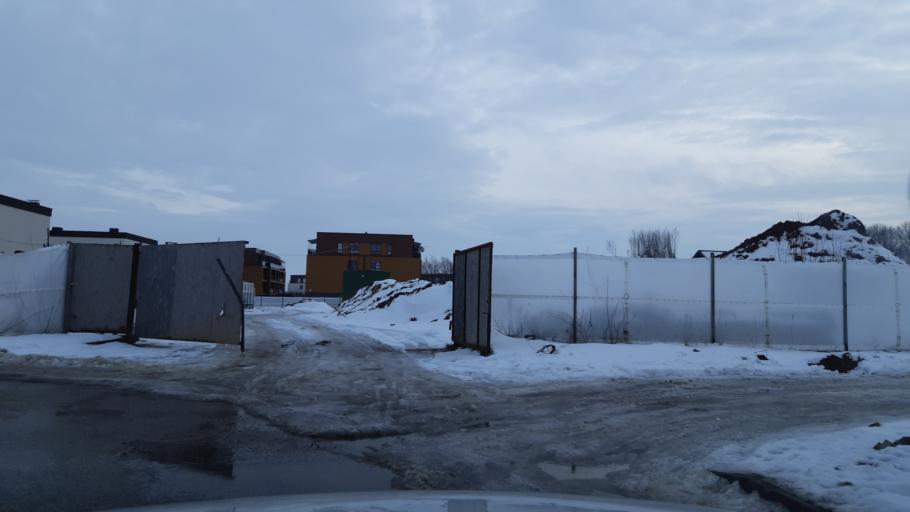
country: LT
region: Kauno apskritis
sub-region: Kauno rajonas
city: Garliava
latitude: 54.8397
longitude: 23.9020
